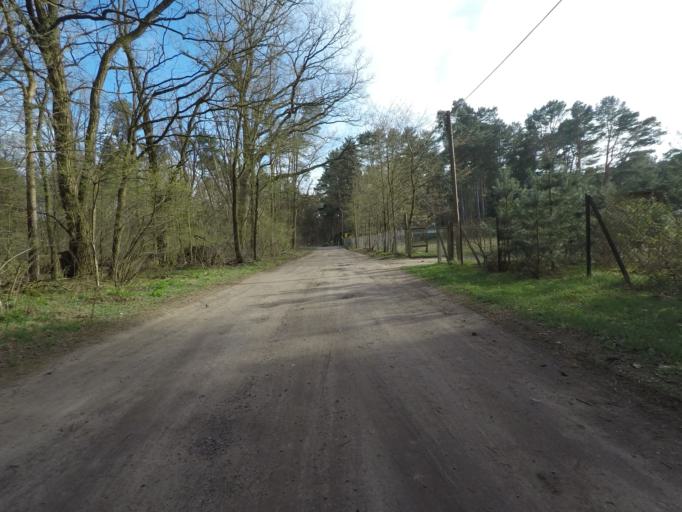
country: DE
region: Brandenburg
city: Marienwerder
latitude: 52.8516
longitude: 13.6531
